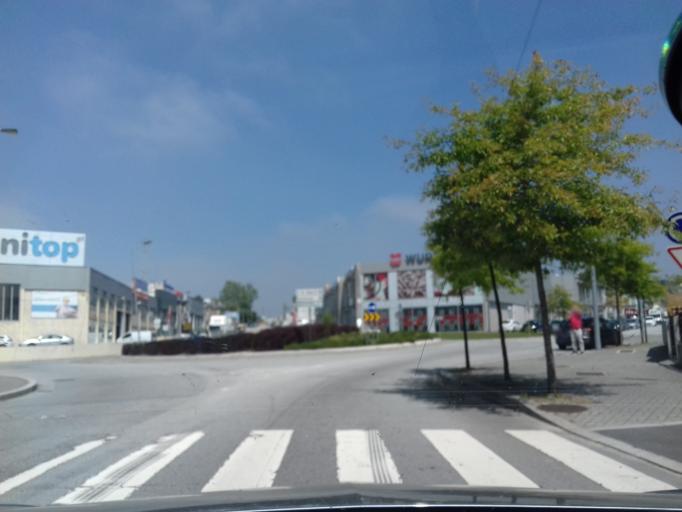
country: PT
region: Porto
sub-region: Vila Nova de Gaia
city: Canelas
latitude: 41.0893
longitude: -8.6040
